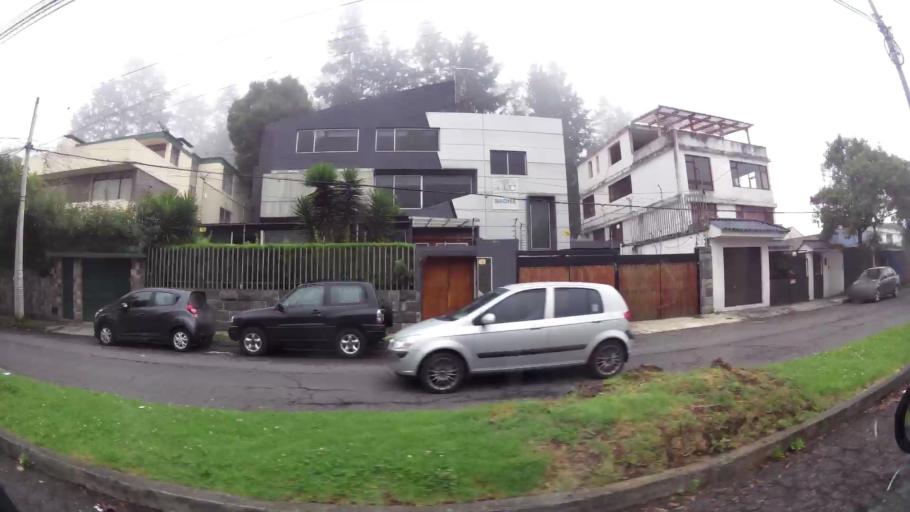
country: EC
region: Pichincha
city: Quito
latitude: -0.2053
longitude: -78.4804
